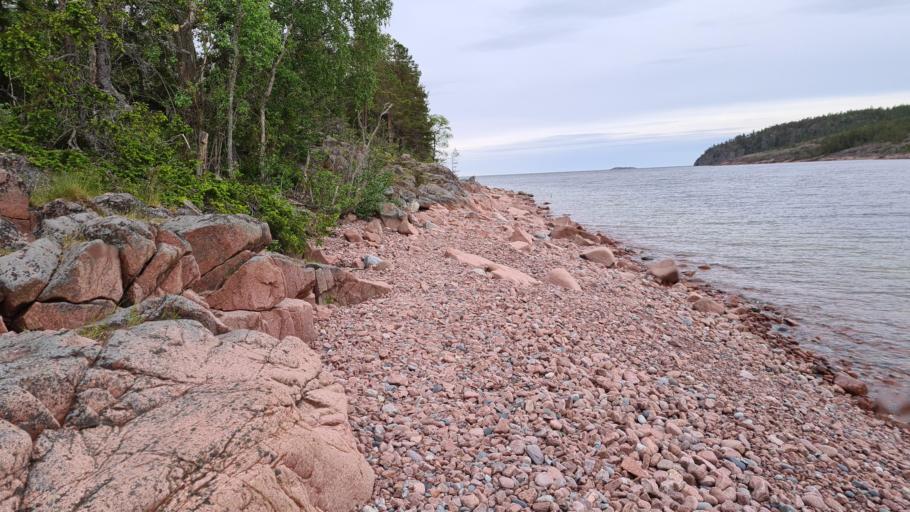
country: SE
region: Vaesternorrland
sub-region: OErnskoeldsviks Kommun
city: Kopmanholmen
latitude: 62.9706
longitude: 18.5198
